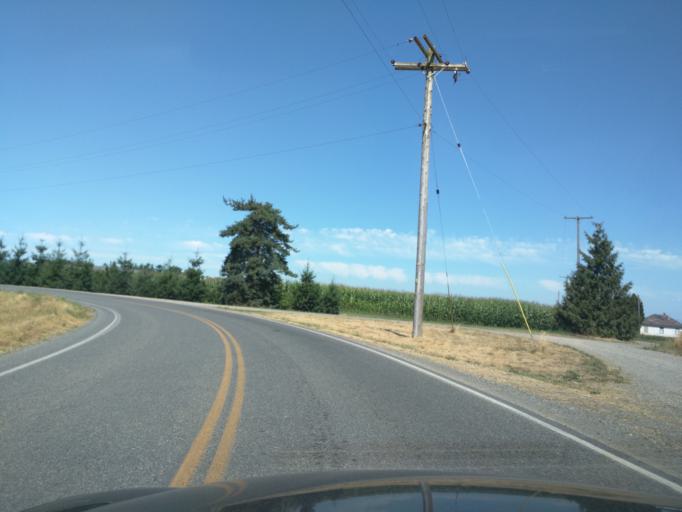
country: US
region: Washington
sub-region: Whatcom County
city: Lynden
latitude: 48.9129
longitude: -122.4088
